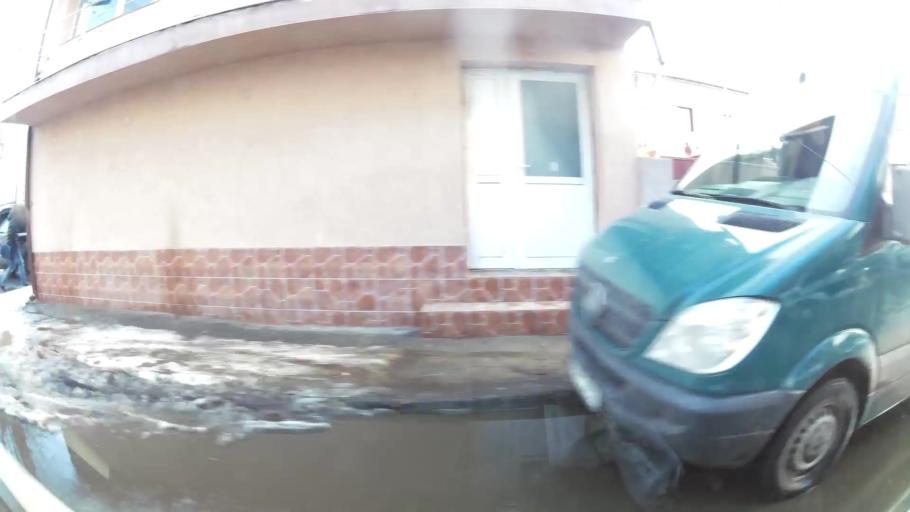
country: RO
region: Bucuresti
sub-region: Municipiul Bucuresti
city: Bucuresti
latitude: 44.3890
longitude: 26.0831
